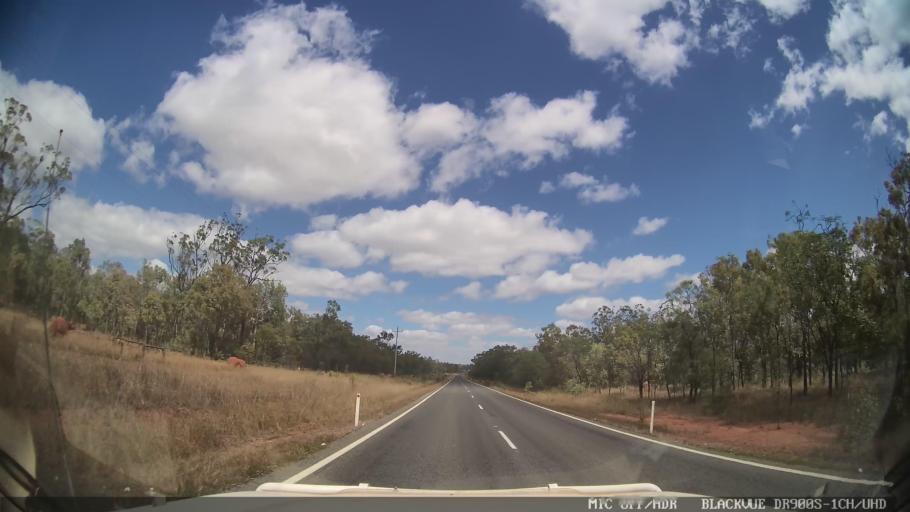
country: AU
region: Queensland
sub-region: Tablelands
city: Ravenshoe
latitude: -18.0284
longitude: 144.8700
